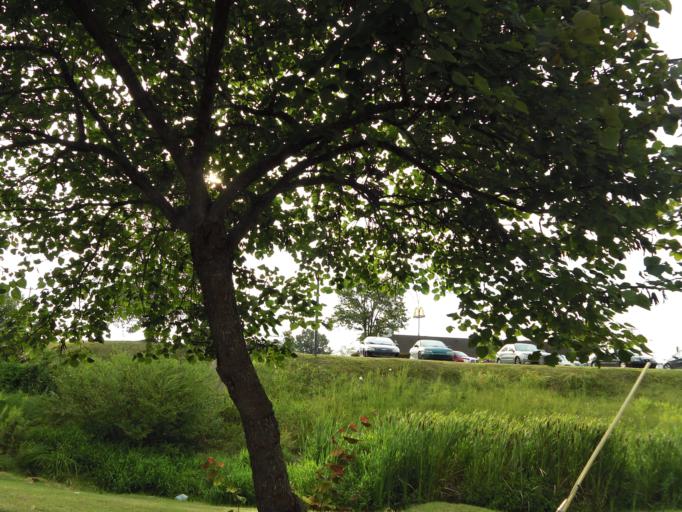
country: US
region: Tennessee
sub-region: Dickson County
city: Burns
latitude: 36.0214
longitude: -87.3361
